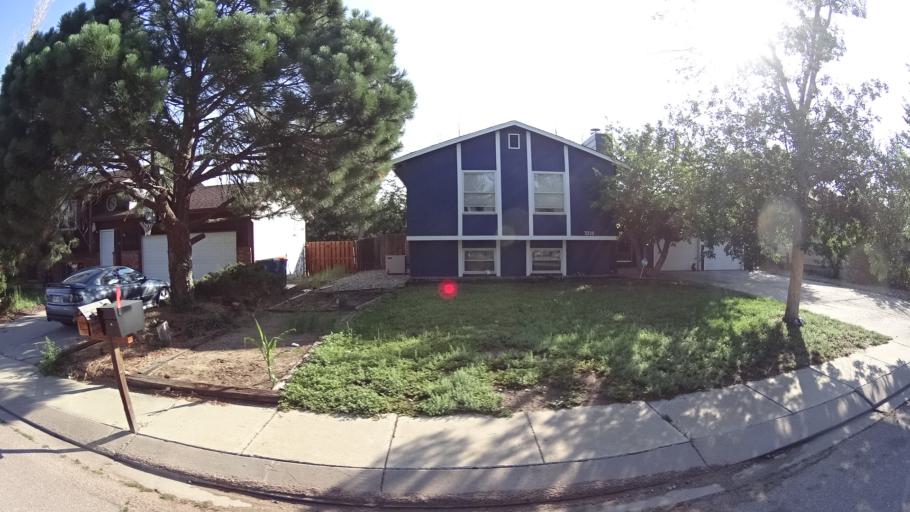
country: US
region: Colorado
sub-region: El Paso County
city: Black Forest
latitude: 38.9443
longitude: -104.7647
